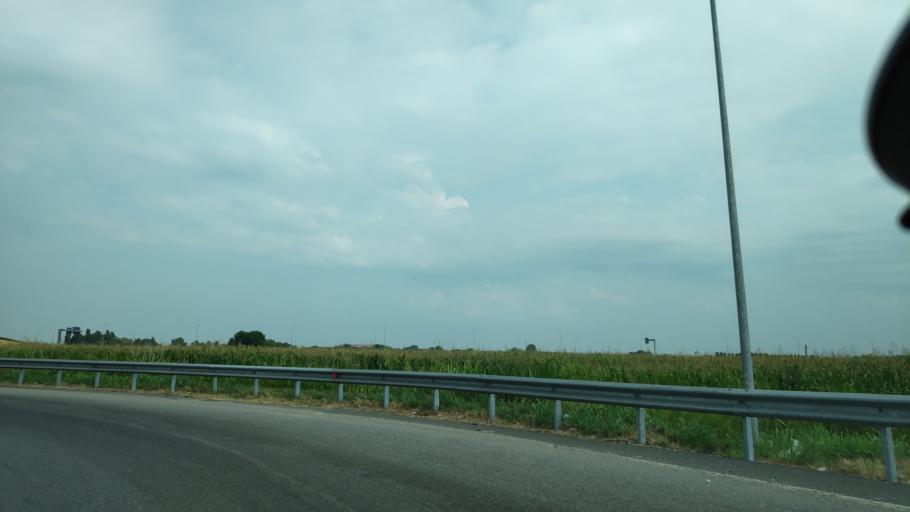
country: IT
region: Lombardy
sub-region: Citta metropolitana di Milano
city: Vizzolo Predabissi
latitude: 45.3466
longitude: 9.3504
